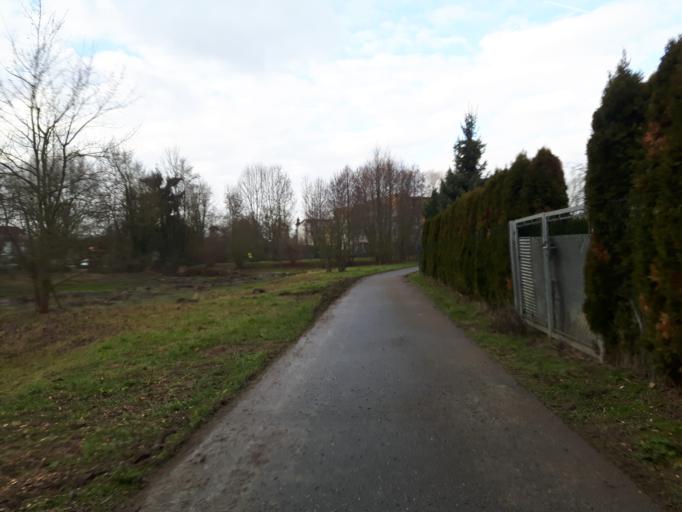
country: DE
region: Baden-Wuerttemberg
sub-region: Regierungsbezirk Stuttgart
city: Leingarten
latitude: 49.1460
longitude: 9.1232
